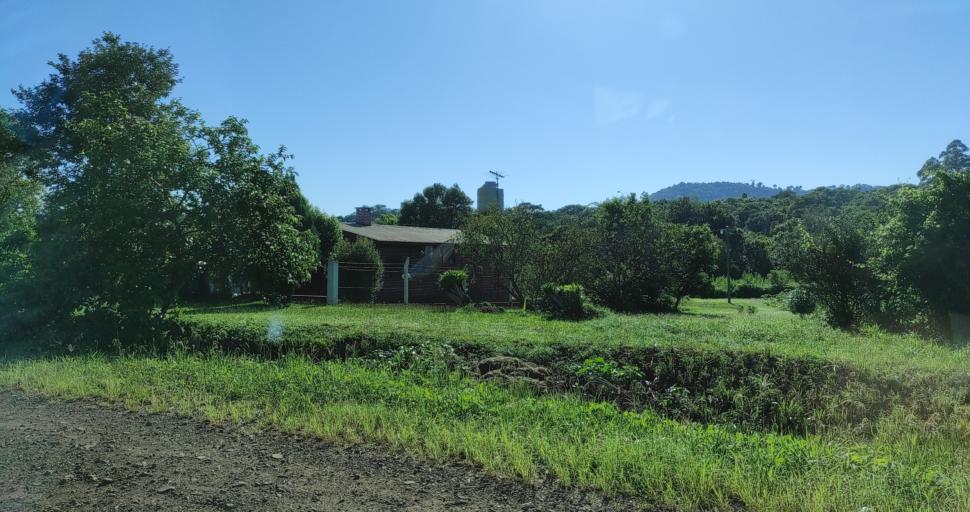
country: AR
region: Misiones
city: El Soberbio
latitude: -27.2756
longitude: -54.1952
